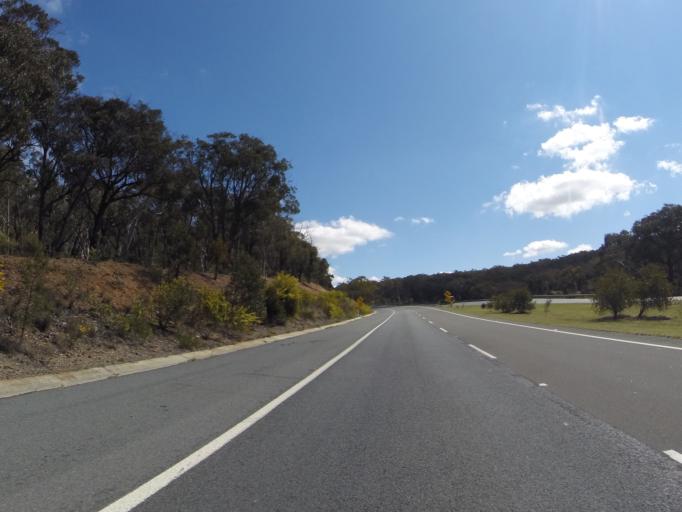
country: AU
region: New South Wales
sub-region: Goulburn Mulwaree
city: Goulburn
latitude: -34.7426
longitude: 149.7641
